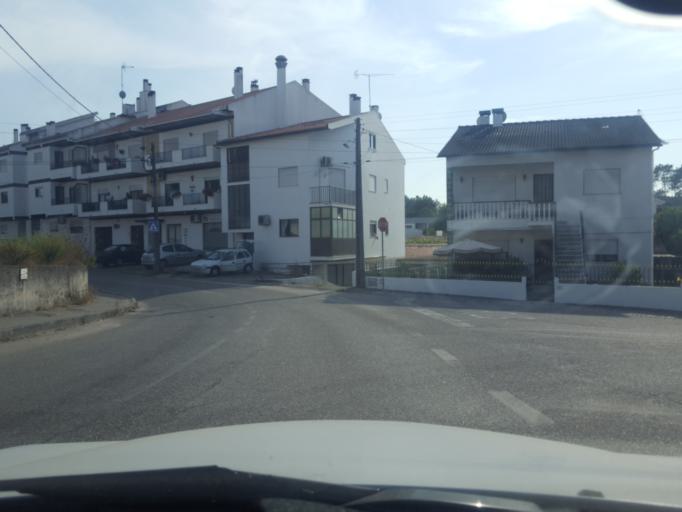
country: PT
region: Leiria
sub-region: Leiria
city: Leiria
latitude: 39.7312
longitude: -8.7629
